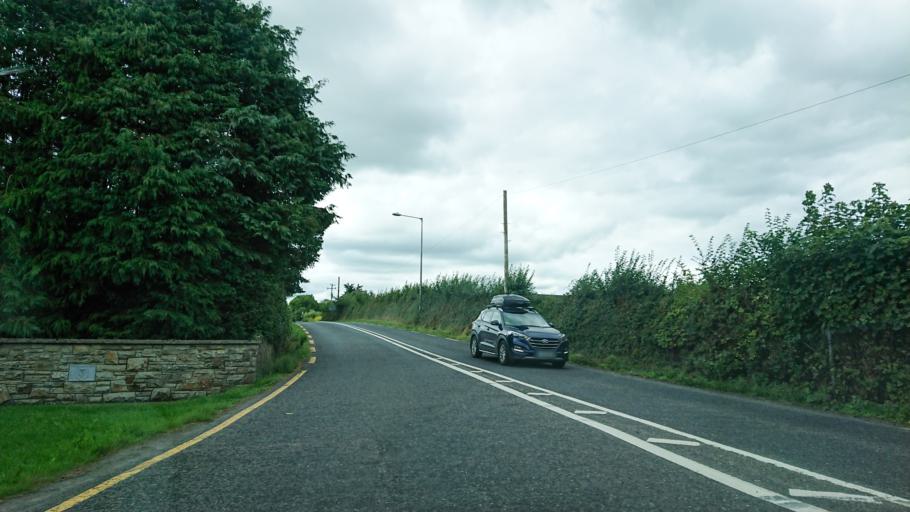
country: IE
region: Munster
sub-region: Waterford
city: Dungarvan
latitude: 52.1131
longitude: -7.5954
